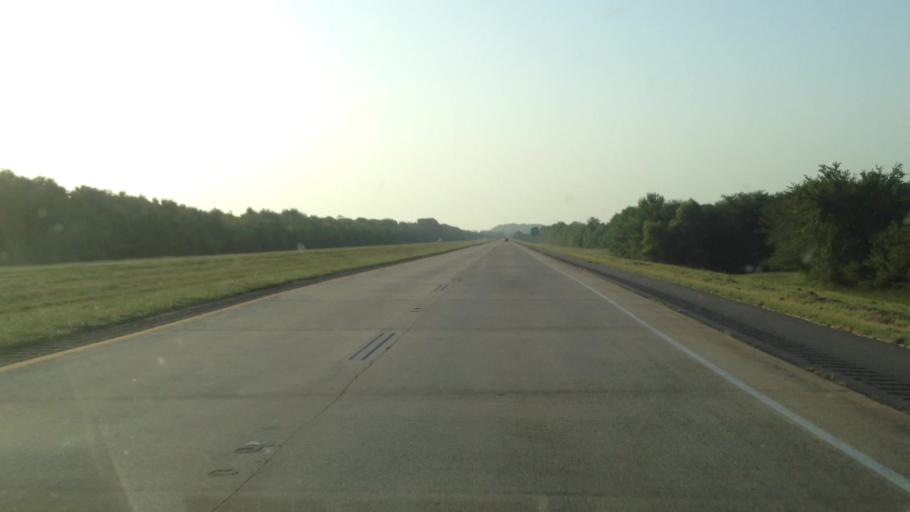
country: US
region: Louisiana
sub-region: Grant Parish
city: Colfax
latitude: 31.5069
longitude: -92.8865
